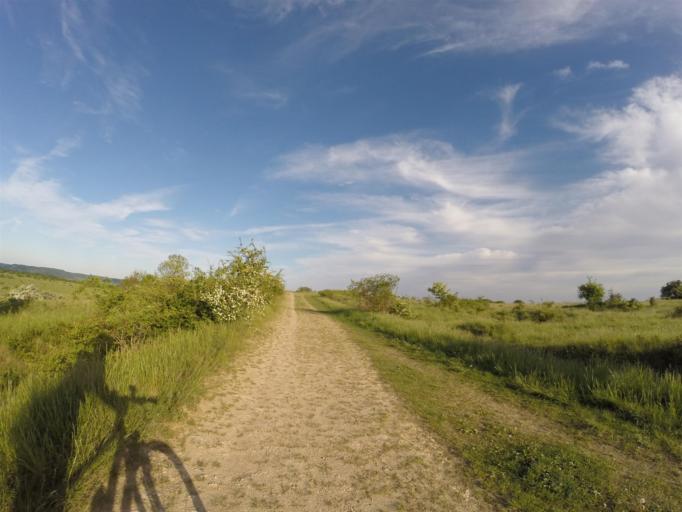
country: DE
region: Thuringia
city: Jena
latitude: 50.9500
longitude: 11.5727
